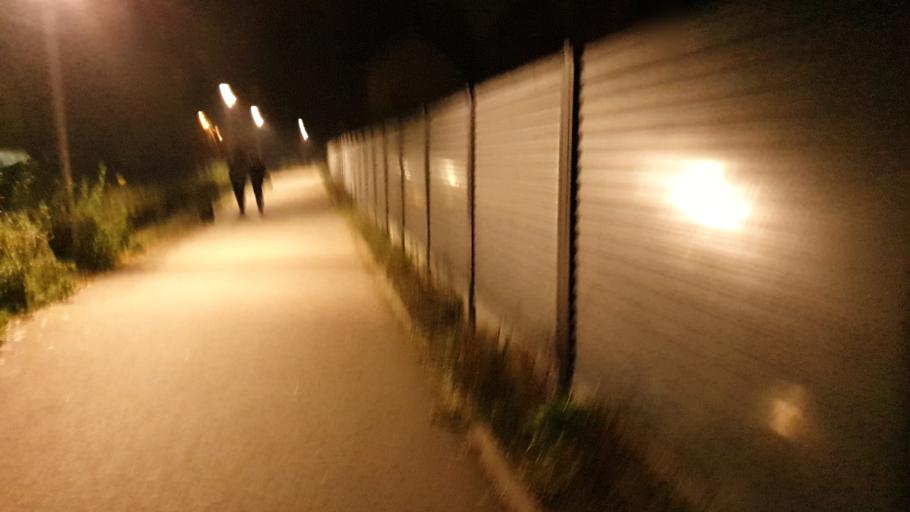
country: PL
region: Masovian Voivodeship
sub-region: Warszawa
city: Wesola
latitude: 52.2195
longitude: 21.2364
